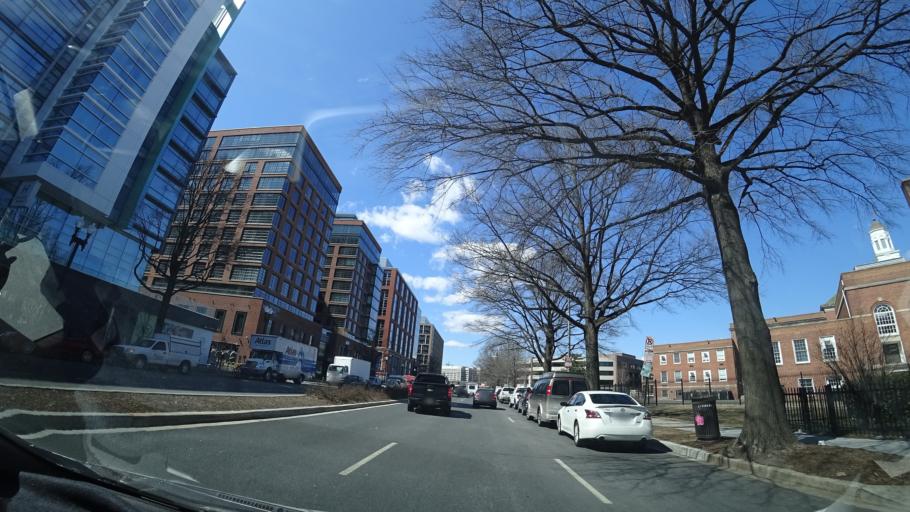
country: US
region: Washington, D.C.
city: Washington, D.C.
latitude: 38.8790
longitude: -77.0232
